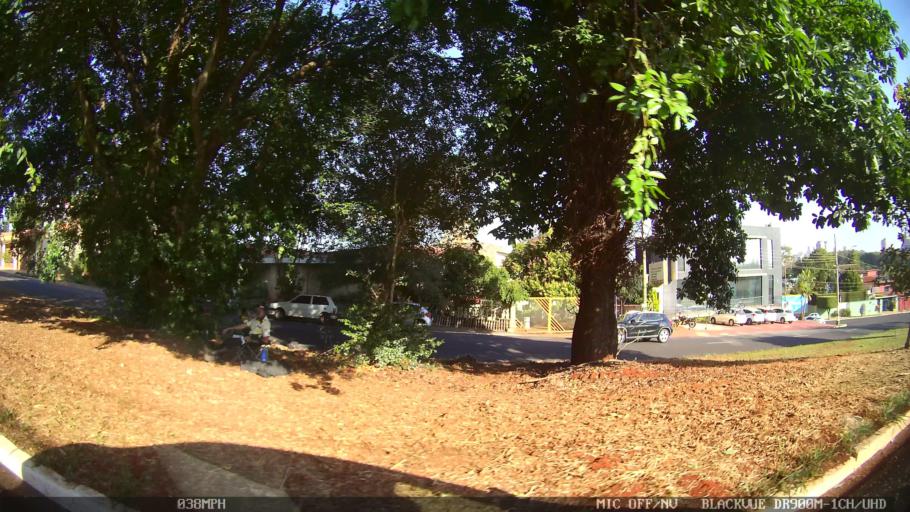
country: BR
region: Sao Paulo
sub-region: Ribeirao Preto
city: Ribeirao Preto
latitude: -21.2060
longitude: -47.7856
